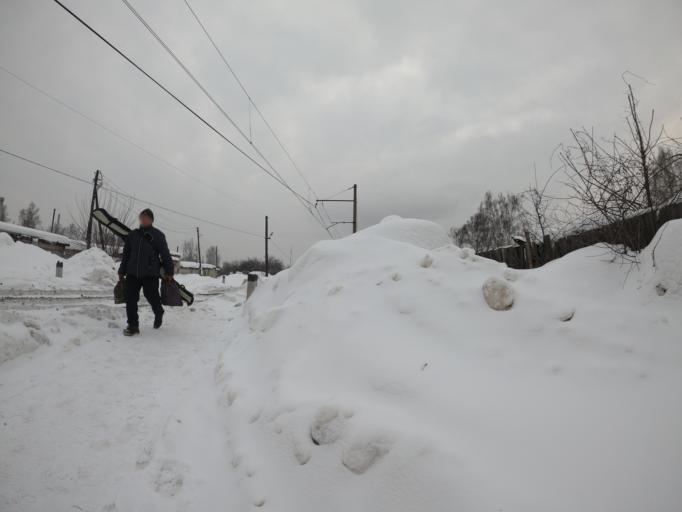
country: RU
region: Moskovskaya
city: Elektrogorsk
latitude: 55.8741
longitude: 38.7875
